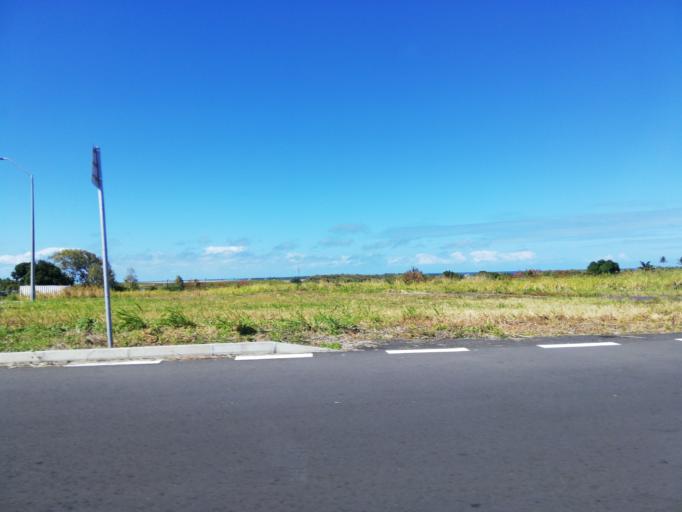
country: MU
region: Grand Port
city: Beau Vallon
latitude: -20.4421
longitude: 57.6901
